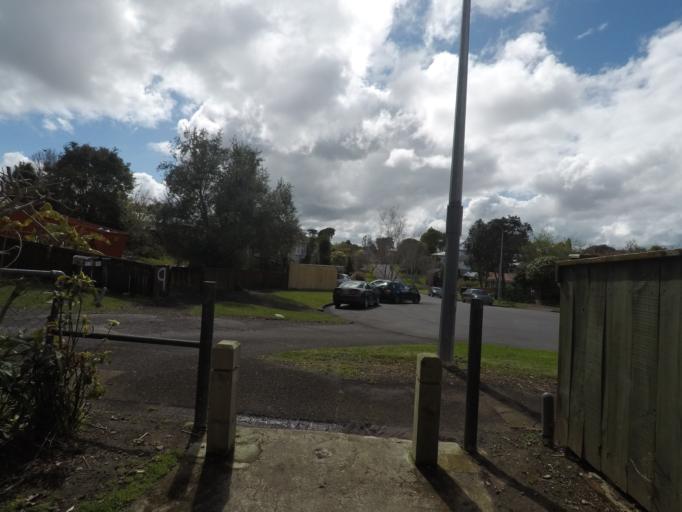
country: NZ
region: Auckland
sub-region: Auckland
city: Rosebank
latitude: -36.8872
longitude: 174.6749
